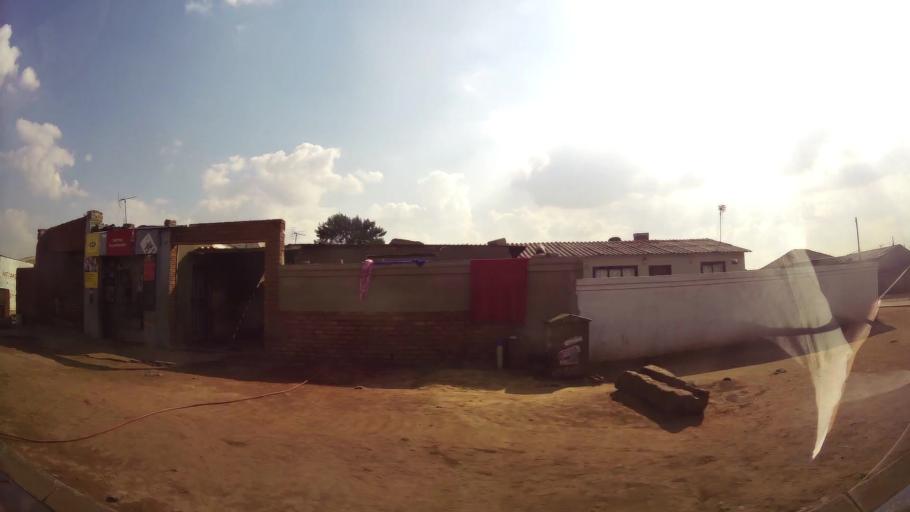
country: ZA
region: Gauteng
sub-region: Ekurhuleni Metropolitan Municipality
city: Germiston
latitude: -26.3052
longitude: 28.1512
